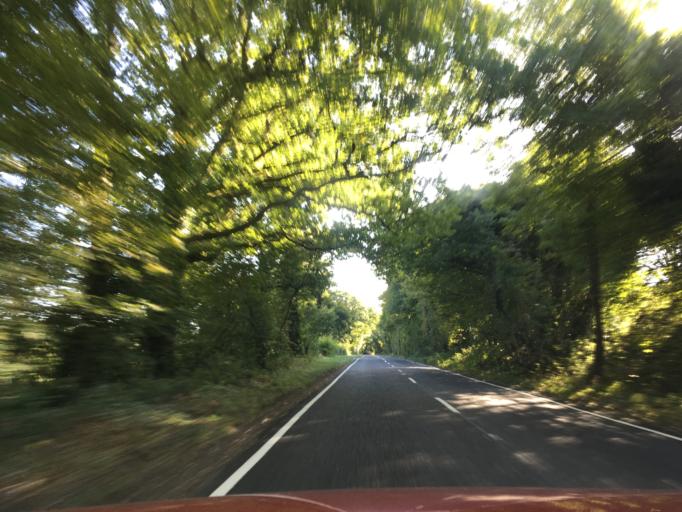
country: GB
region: England
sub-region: Hampshire
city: Four Marks
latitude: 51.0252
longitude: -1.0772
